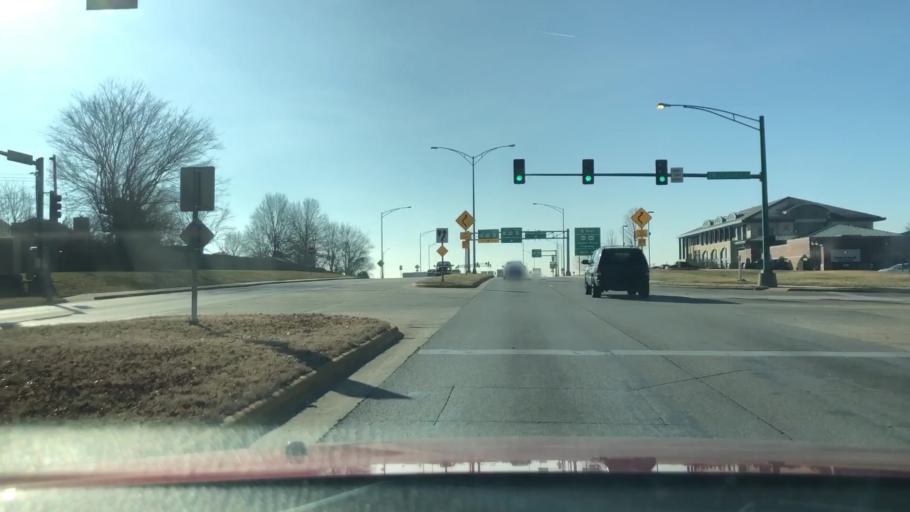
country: US
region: Missouri
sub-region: Greene County
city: Battlefield
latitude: 37.1462
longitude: -93.3193
